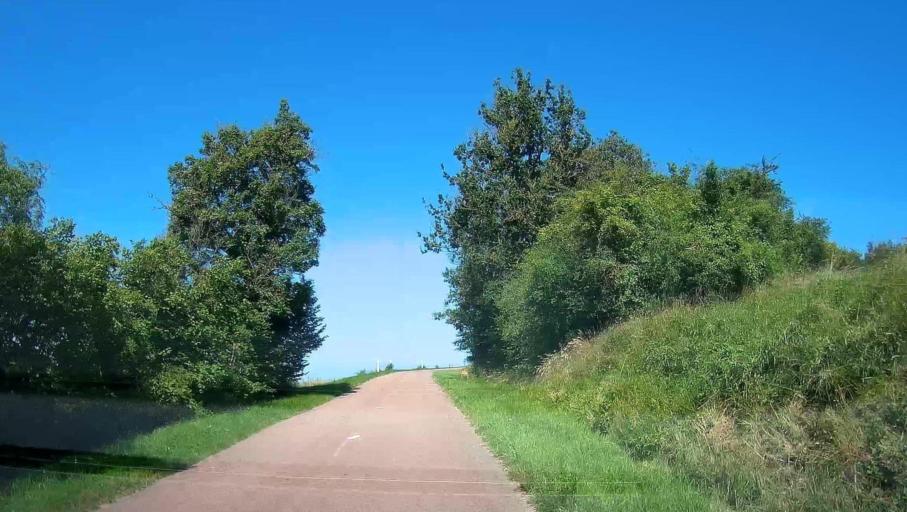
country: FR
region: Bourgogne
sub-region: Departement de la Cote-d'Or
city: Nolay
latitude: 46.9780
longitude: 4.6612
